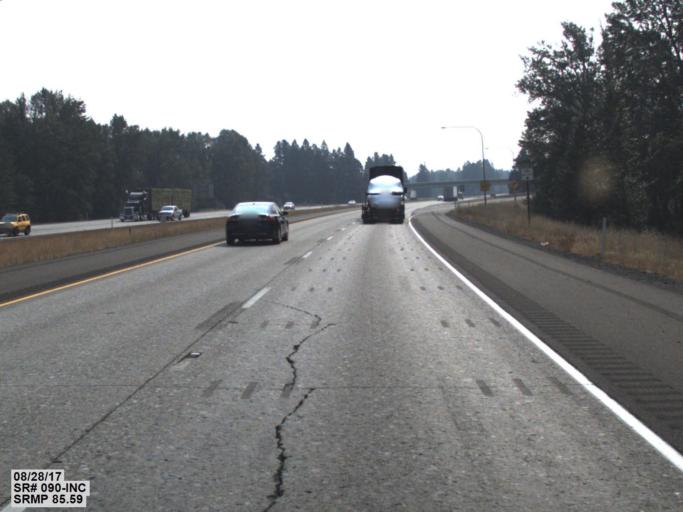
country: US
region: Washington
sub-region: Kittitas County
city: Cle Elum
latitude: 47.1851
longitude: -120.9084
